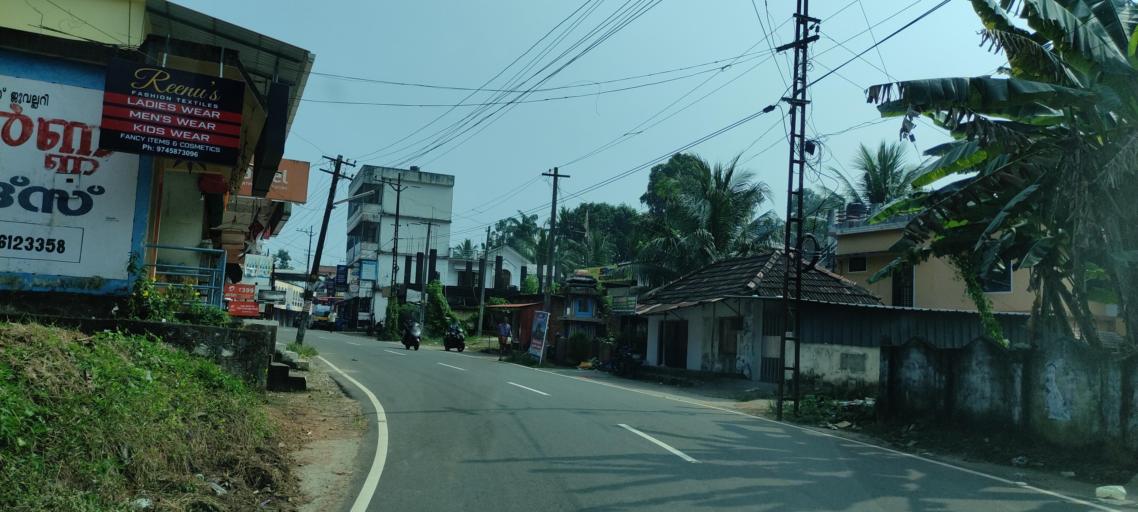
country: IN
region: Kerala
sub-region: Pattanamtitta
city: Adur
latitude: 9.2368
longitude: 76.6958
